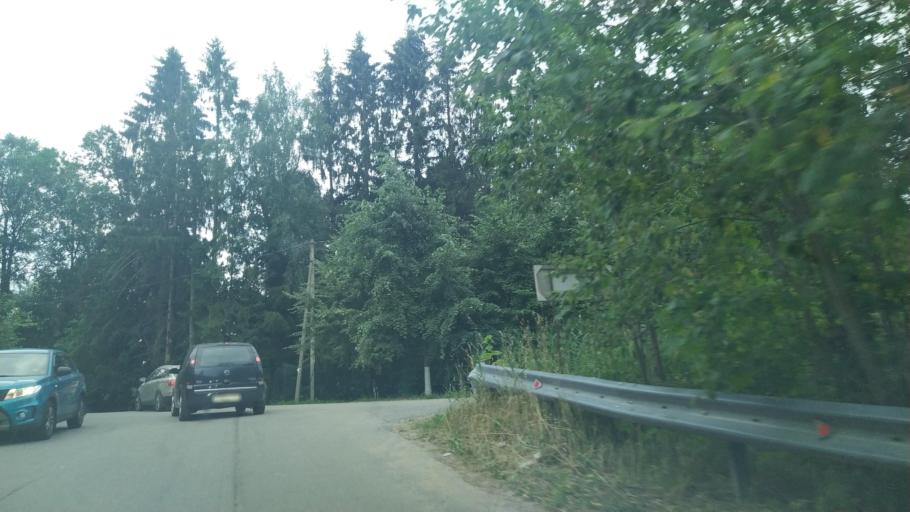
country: RU
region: Leningrad
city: Toksovo
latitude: 60.1664
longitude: 30.5373
